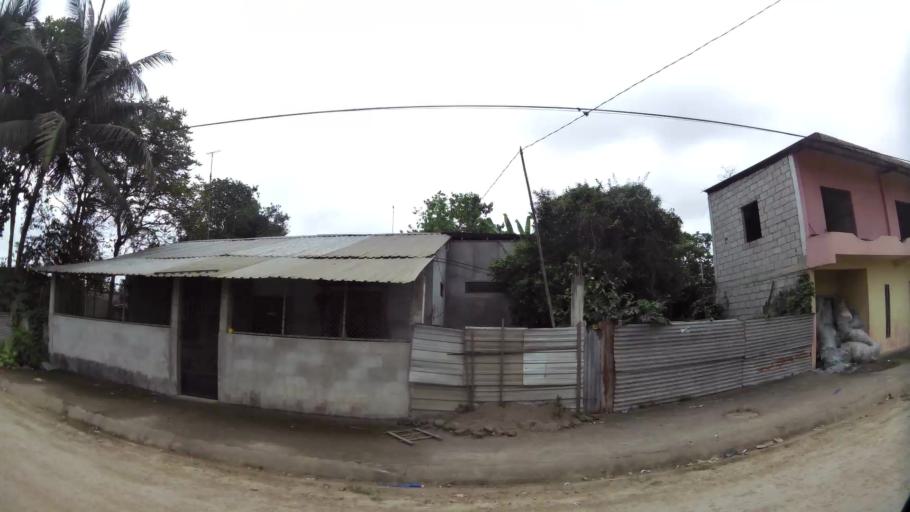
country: EC
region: El Oro
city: Pasaje
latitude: -3.2358
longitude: -79.8249
